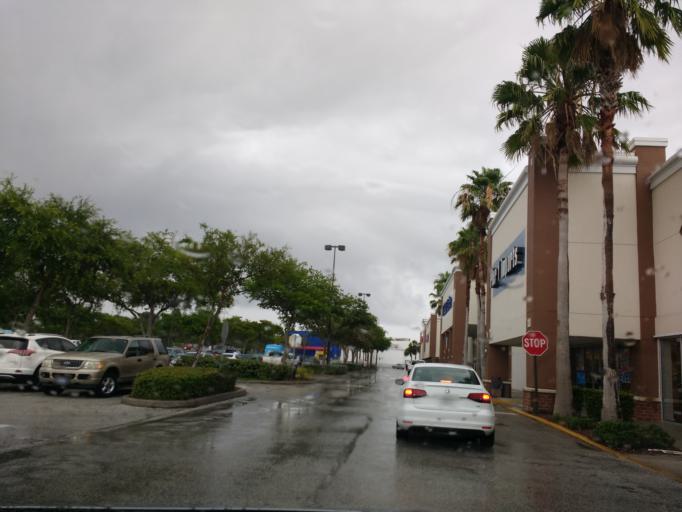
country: US
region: Florida
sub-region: Pinellas County
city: Kenneth City
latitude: 27.7881
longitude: -82.7263
